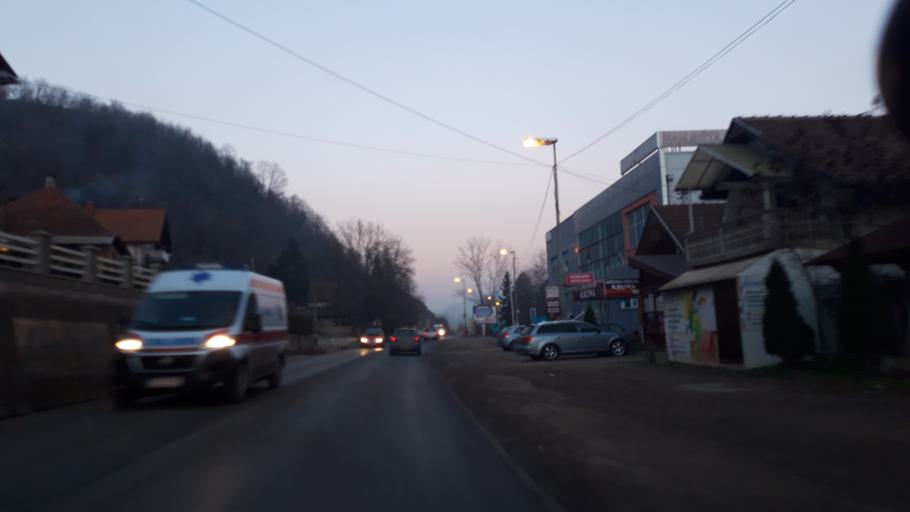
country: BA
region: Republika Srpska
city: Zvornik
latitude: 44.4054
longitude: 19.1195
